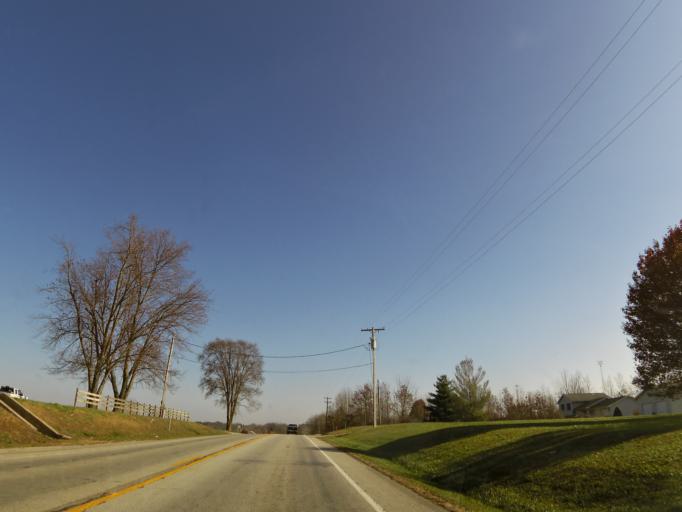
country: US
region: Indiana
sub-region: Fayette County
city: Connersville
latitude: 39.6369
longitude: -85.1834
